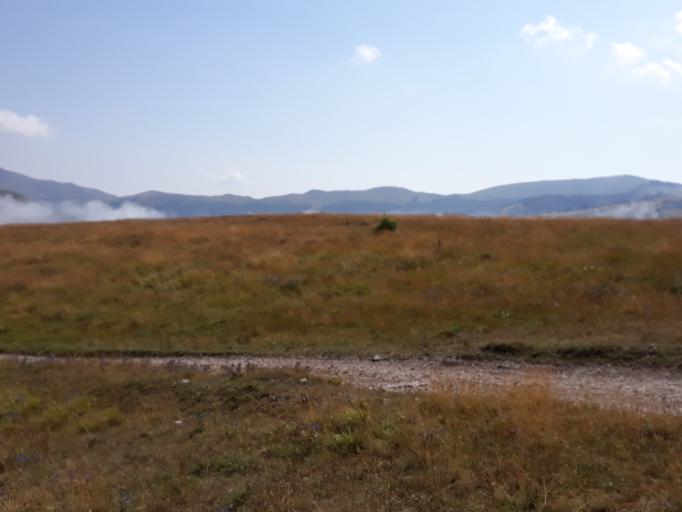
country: IT
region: Latium
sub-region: Provincia di Rieti
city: Accumoli
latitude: 42.7659
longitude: 13.1923
